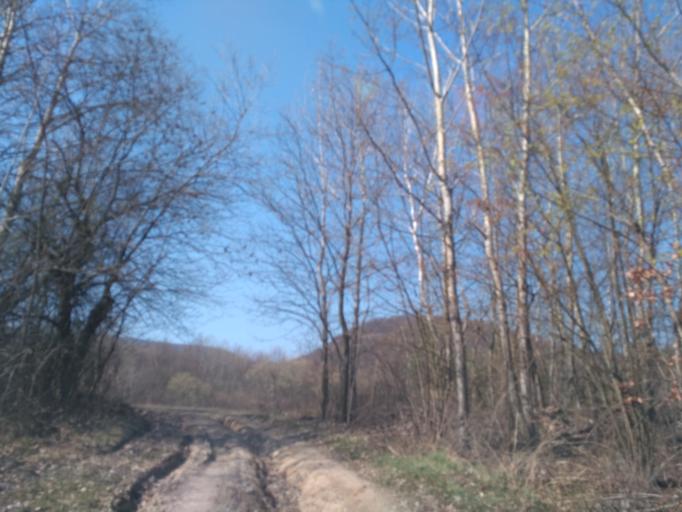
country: SK
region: Presovsky
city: Vranov nad Topl'ou
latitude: 48.8232
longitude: 21.6067
